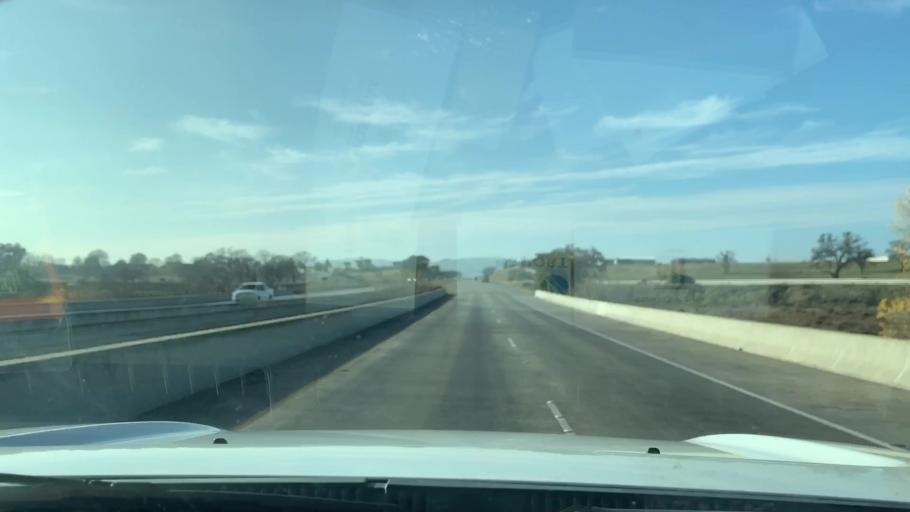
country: US
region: California
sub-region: San Luis Obispo County
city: Paso Robles
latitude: 35.6446
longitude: -120.6454
